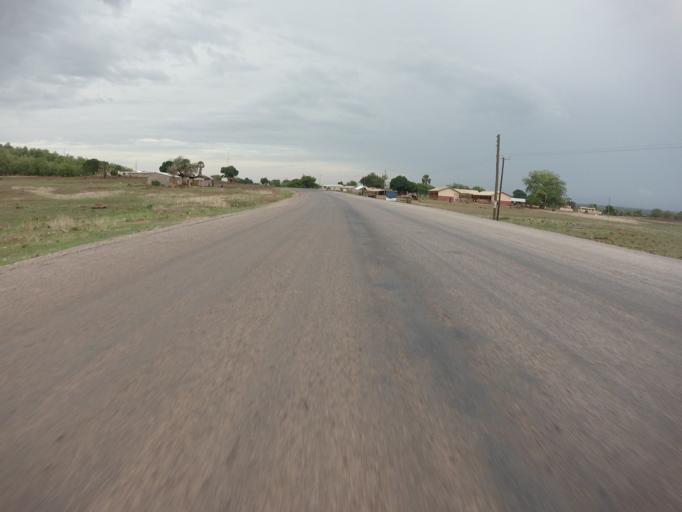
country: GH
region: Upper East
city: Bolgatanga
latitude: 10.8437
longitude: -0.6867
